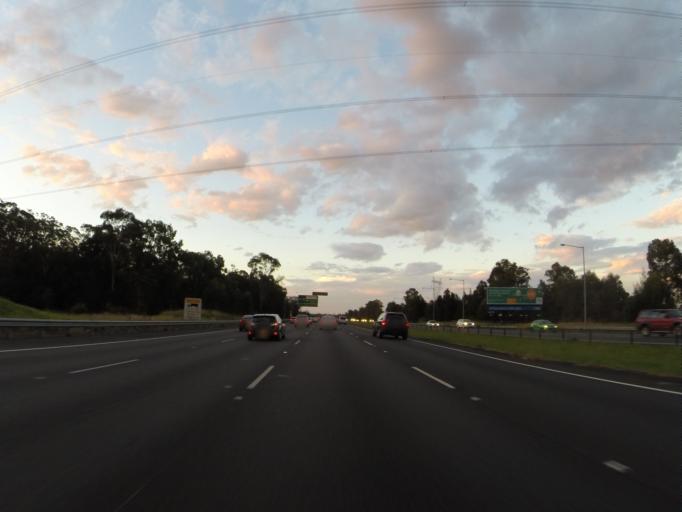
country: AU
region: New South Wales
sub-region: Campbelltown Municipality
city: Glenfield
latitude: -33.9642
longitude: 150.8751
